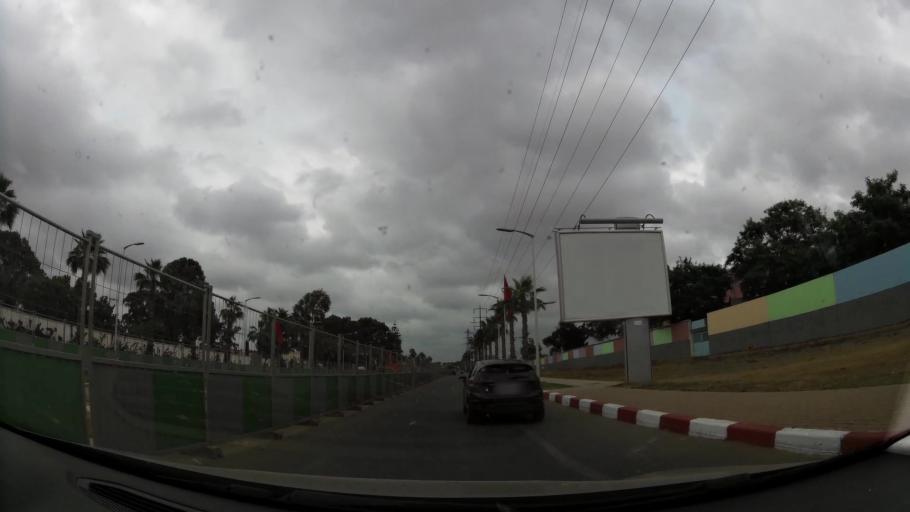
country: MA
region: Rabat-Sale-Zemmour-Zaer
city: Sale
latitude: 34.0346
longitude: -6.7958
